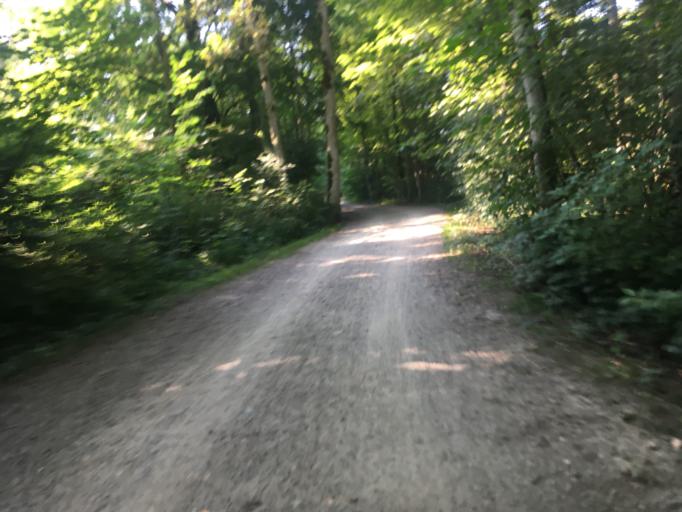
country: CH
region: Bern
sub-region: Emmental District
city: Oberburg
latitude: 47.0353
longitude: 7.6357
